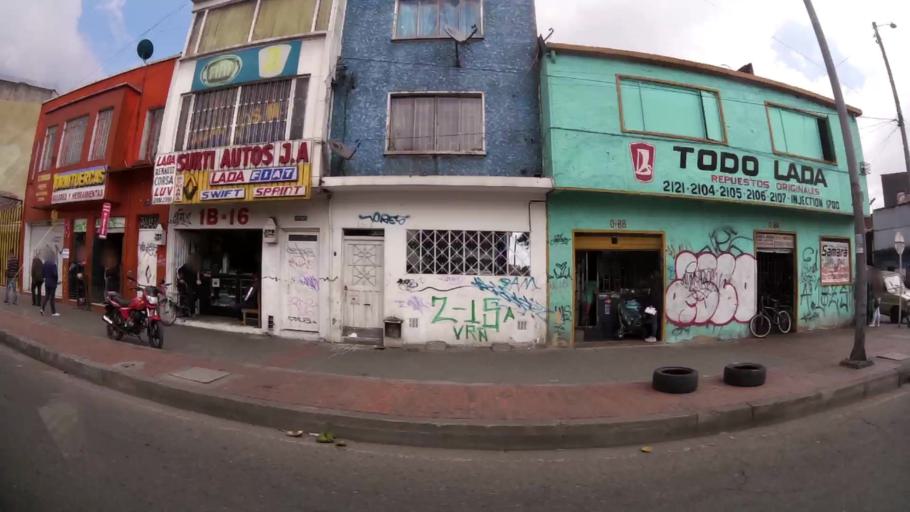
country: CO
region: Bogota D.C.
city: Bogota
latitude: 4.5926
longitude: -74.0881
